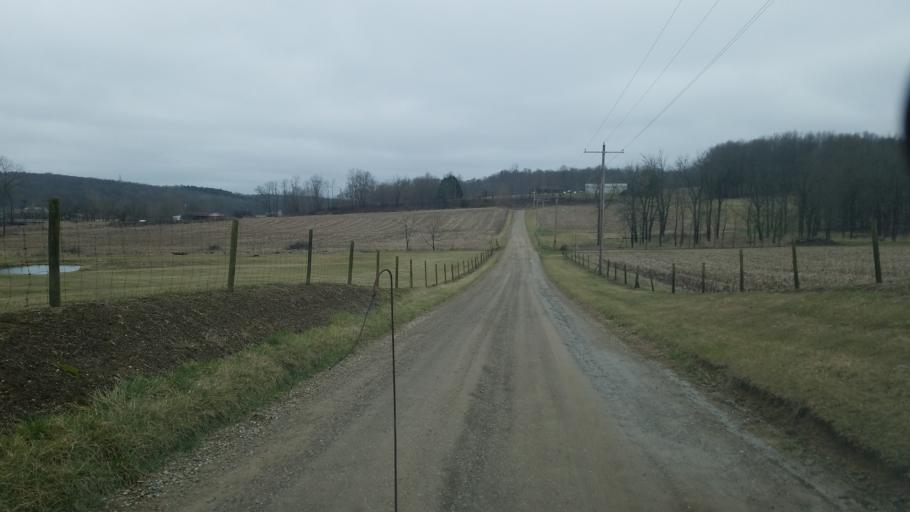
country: US
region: Ohio
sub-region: Knox County
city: Gambier
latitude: 40.4618
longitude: -82.4085
